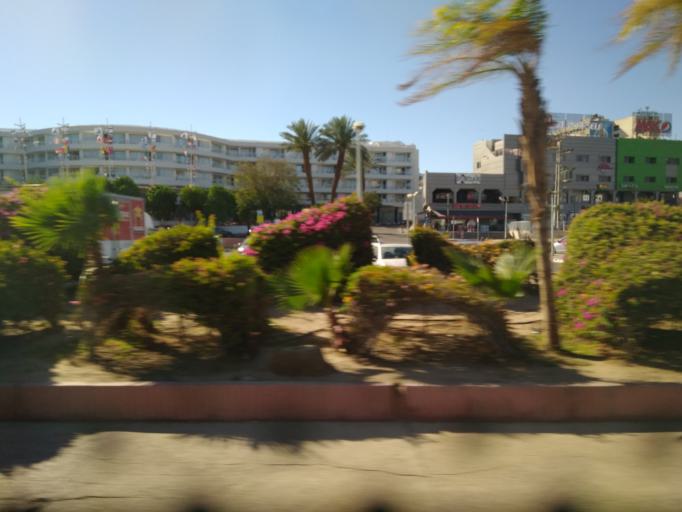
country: IL
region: Southern District
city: Eilat
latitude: 29.5501
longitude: 34.9529
